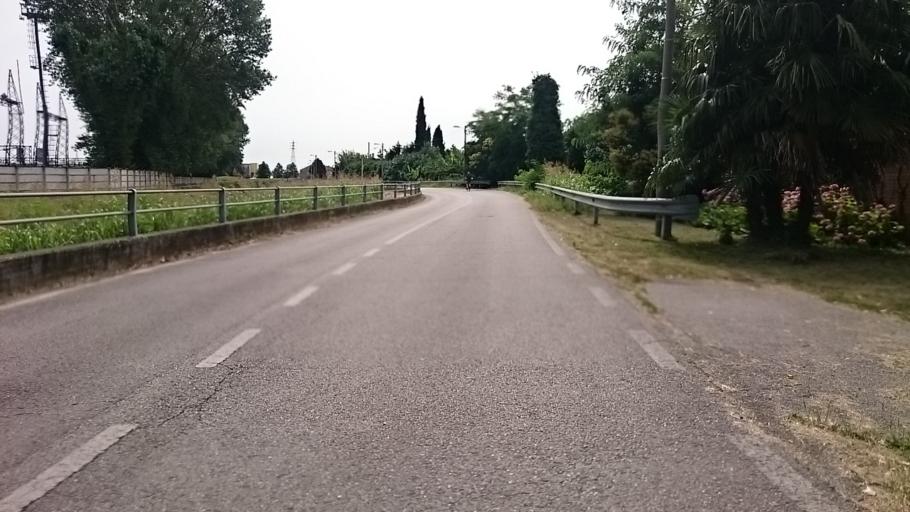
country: IT
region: Veneto
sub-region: Provincia di Venezia
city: Mestre
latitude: 45.4573
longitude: 12.2038
